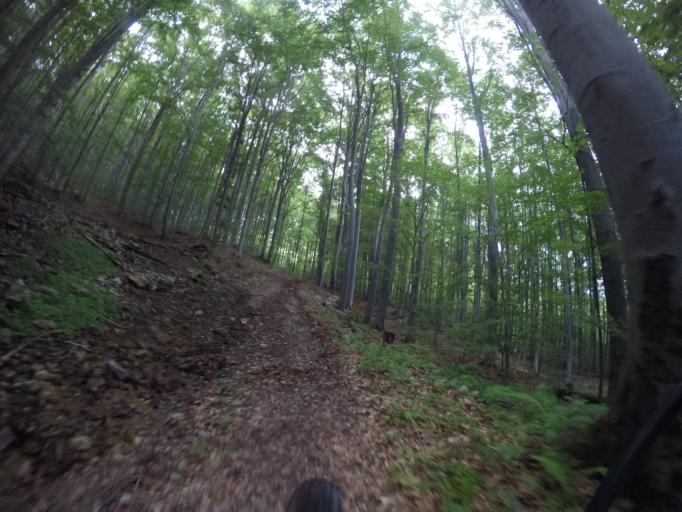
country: SK
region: Kosicky
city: Gelnica
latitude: 48.9249
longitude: 21.0248
